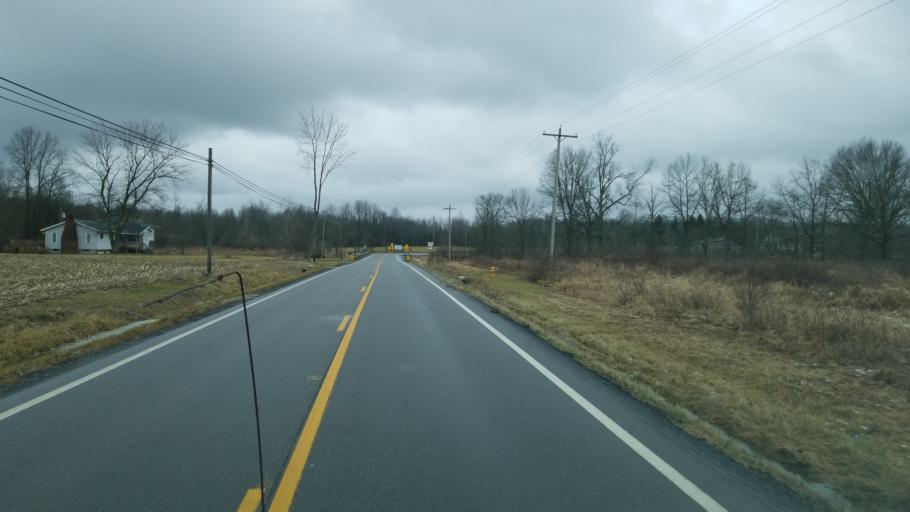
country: US
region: Ohio
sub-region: Trumbull County
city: Champion Heights
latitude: 41.3414
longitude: -80.9545
